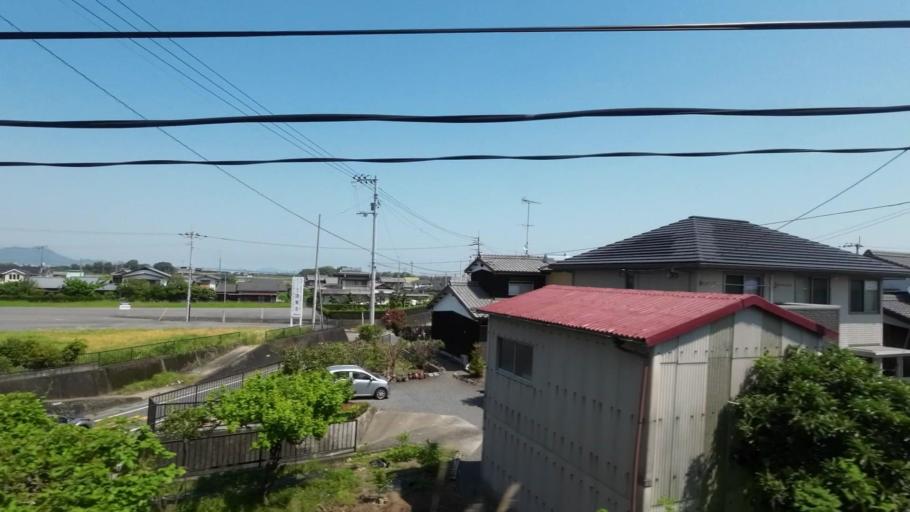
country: JP
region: Ehime
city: Saijo
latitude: 33.8981
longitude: 133.1090
